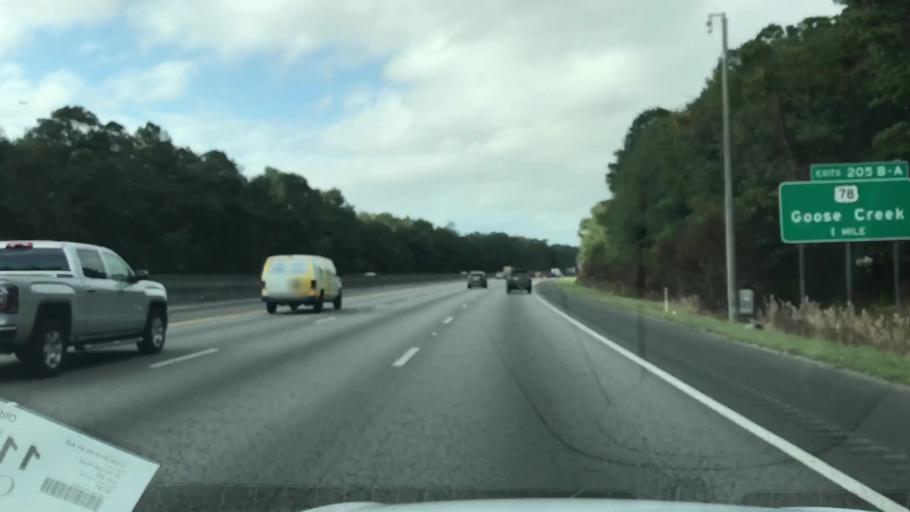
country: US
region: South Carolina
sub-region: Berkeley County
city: Goose Creek
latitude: 32.9623
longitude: -80.0724
